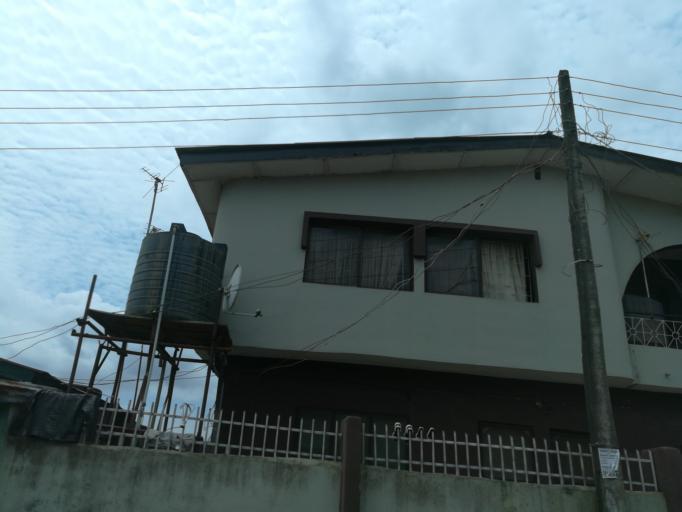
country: NG
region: Lagos
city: Oshodi
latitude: 6.5603
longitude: 3.3305
